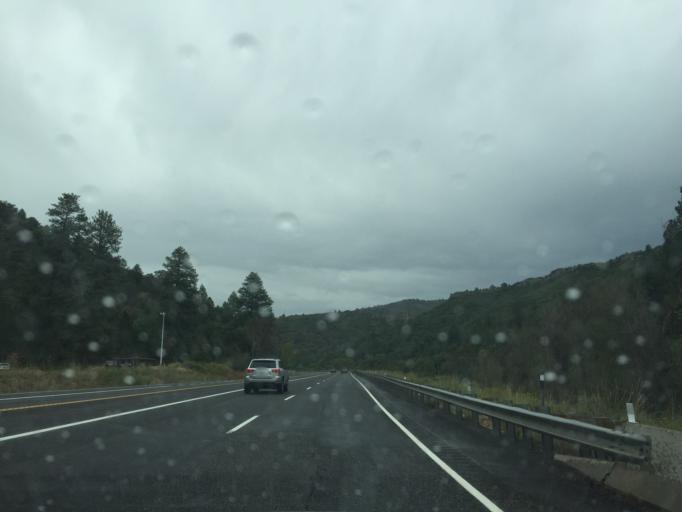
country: US
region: Utah
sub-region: Kane County
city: Kanab
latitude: 37.3789
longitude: -112.5869
